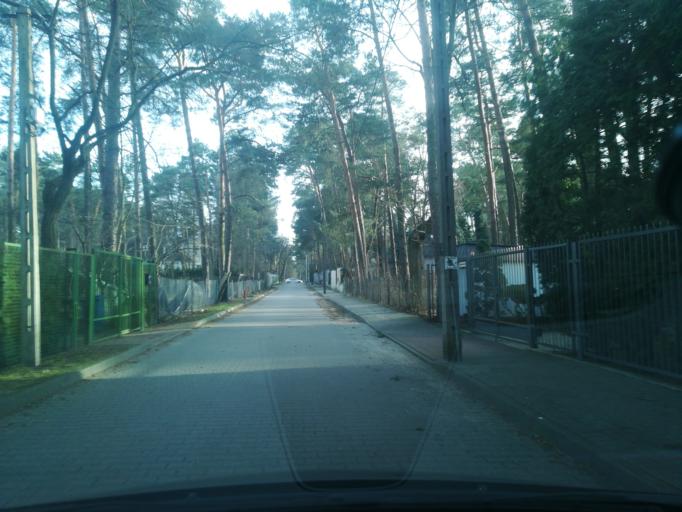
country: PL
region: Masovian Voivodeship
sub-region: Powiat piaseczynski
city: Konstancin-Jeziorna
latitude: 52.0817
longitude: 21.1066
